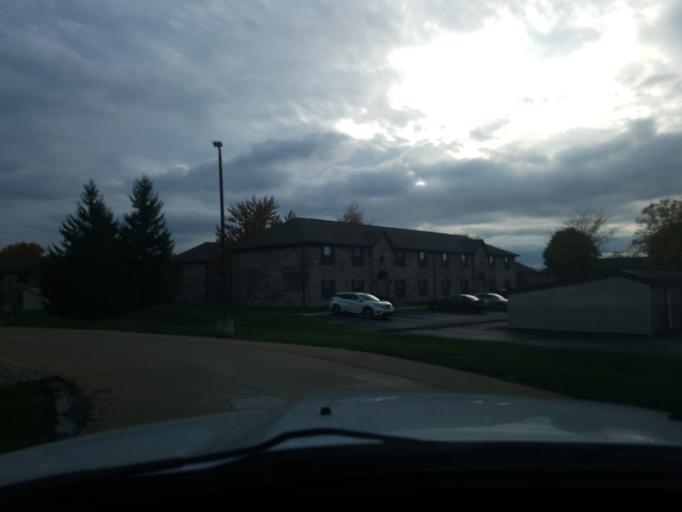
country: US
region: Indiana
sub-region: Shelby County
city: Shelbyville
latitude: 39.5512
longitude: -85.7783
